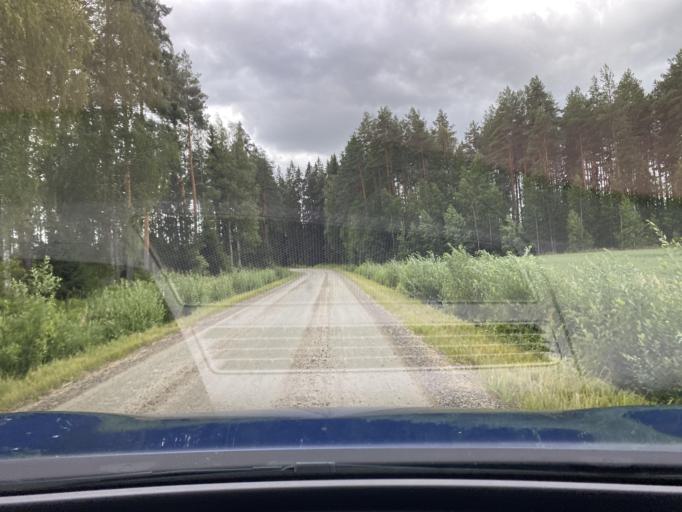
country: FI
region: Pirkanmaa
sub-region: Lounais-Pirkanmaa
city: Punkalaidun
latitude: 61.2030
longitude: 23.1772
